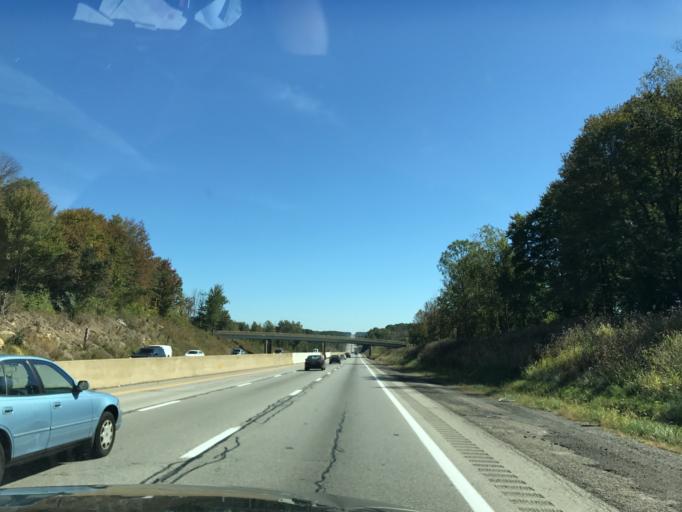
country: US
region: Ohio
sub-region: Perry County
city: Thornport
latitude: 39.9422
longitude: -82.3824
